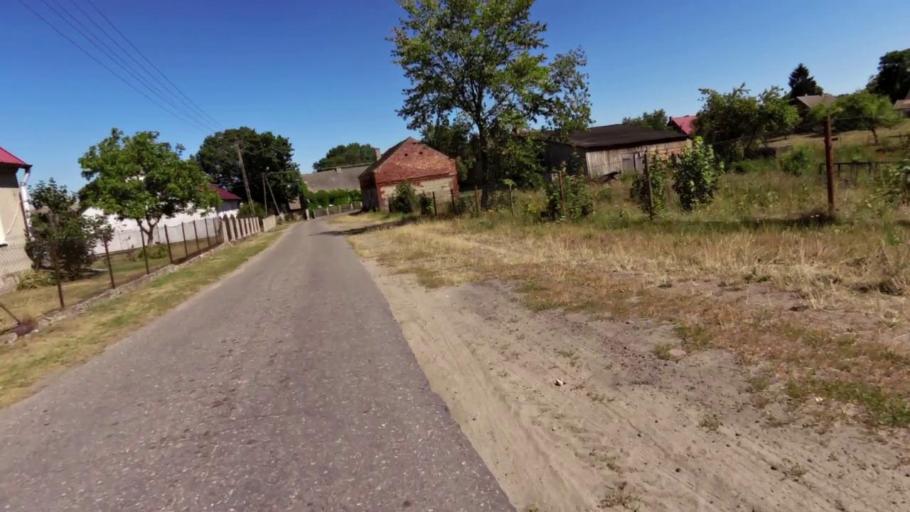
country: PL
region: West Pomeranian Voivodeship
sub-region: Powiat szczecinecki
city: Szczecinek
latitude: 53.6299
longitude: 16.6785
